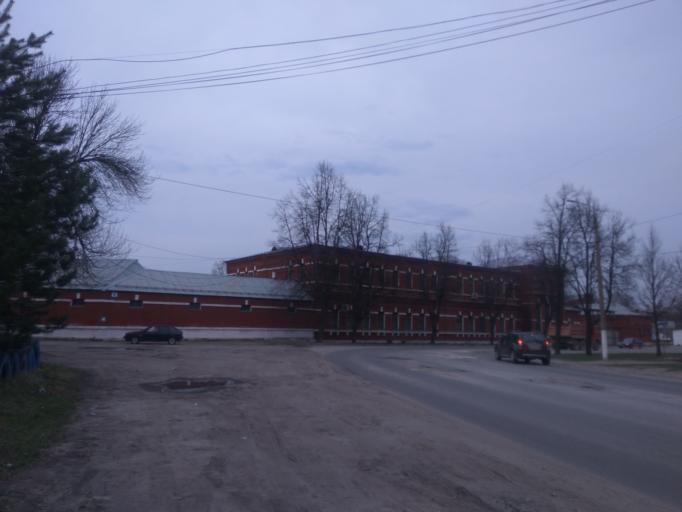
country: RU
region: Vladimir
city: Aleksandrov
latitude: 56.4016
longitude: 38.7115
